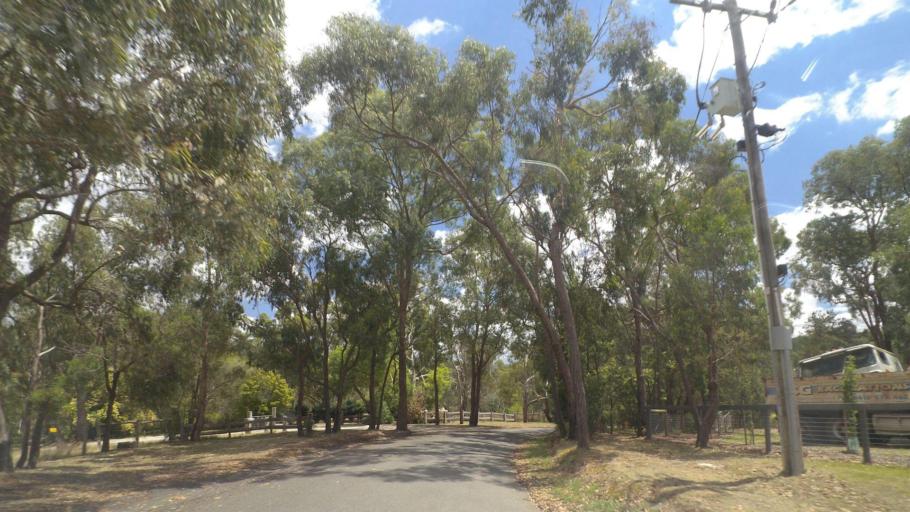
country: AU
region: Victoria
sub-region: Maroondah
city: Croydon Hills
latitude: -37.7618
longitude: 145.2600
